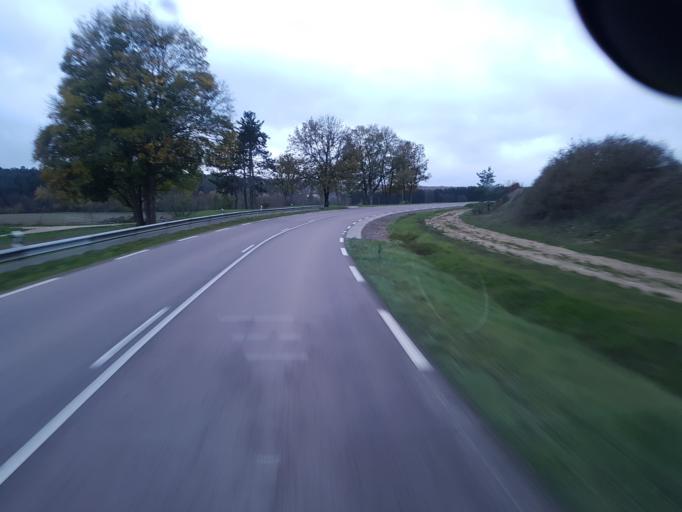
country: FR
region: Champagne-Ardenne
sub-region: Departement de l'Aube
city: Mussy-sur-Seine
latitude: 47.9858
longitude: 4.4866
